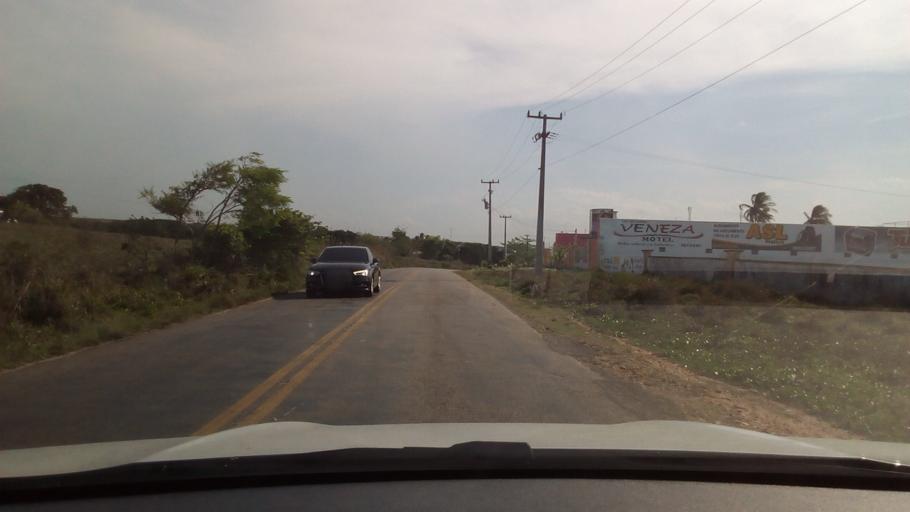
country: BR
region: Rio Grande do Norte
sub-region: Goianinha
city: Goianinha
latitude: -6.2638
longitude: -35.2026
